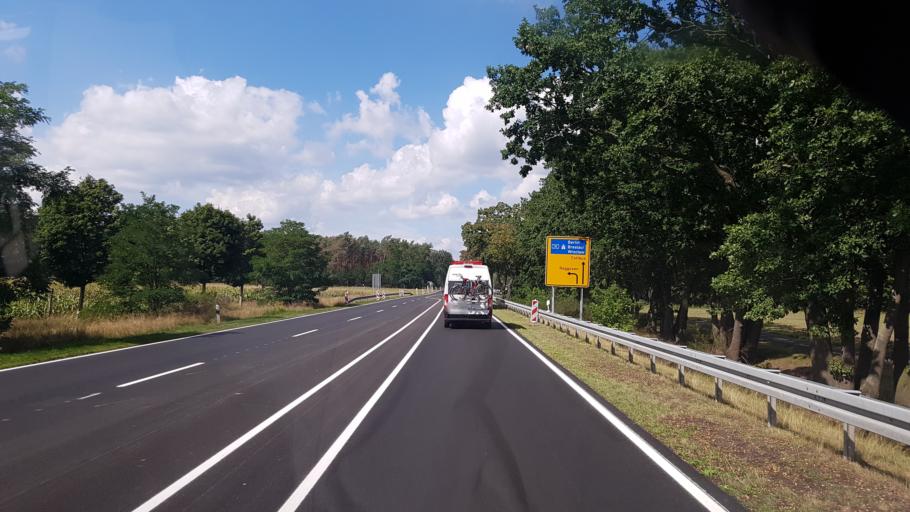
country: DE
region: Brandenburg
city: Heinersbruck
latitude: 51.7067
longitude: 14.4742
